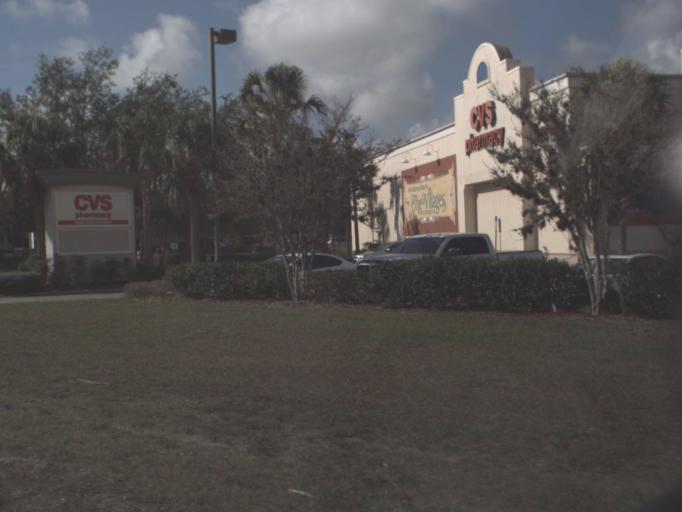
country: US
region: Florida
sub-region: Sumter County
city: The Villages
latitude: 28.9371
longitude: -81.9414
